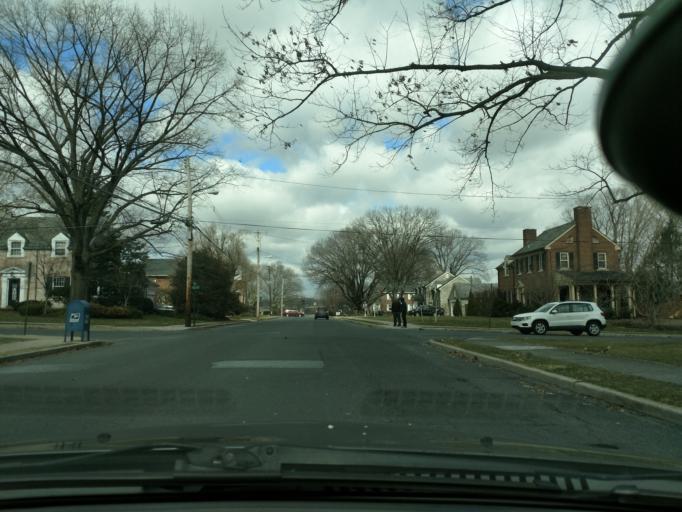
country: US
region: Pennsylvania
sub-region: Lebanon County
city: Lebanon
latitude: 40.3372
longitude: -76.4064
